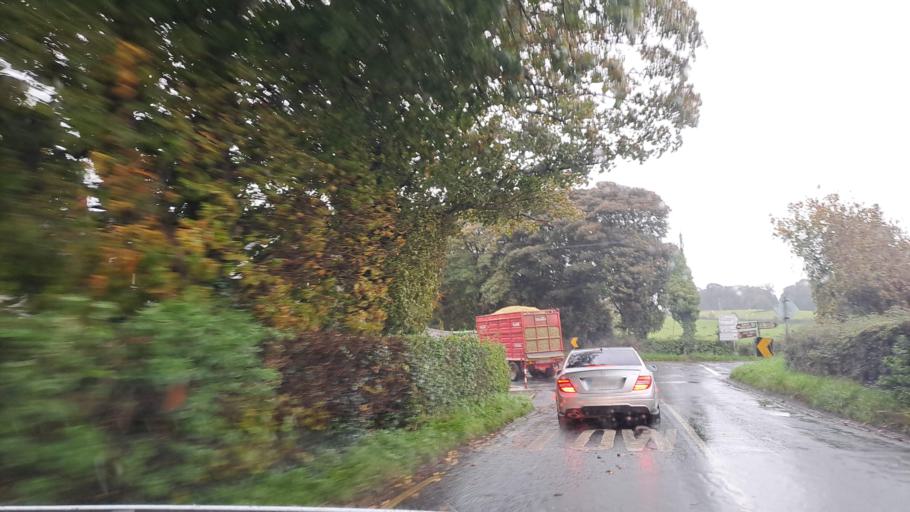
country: IE
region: Ulster
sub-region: County Monaghan
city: Carrickmacross
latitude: 53.9756
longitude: -6.6419
